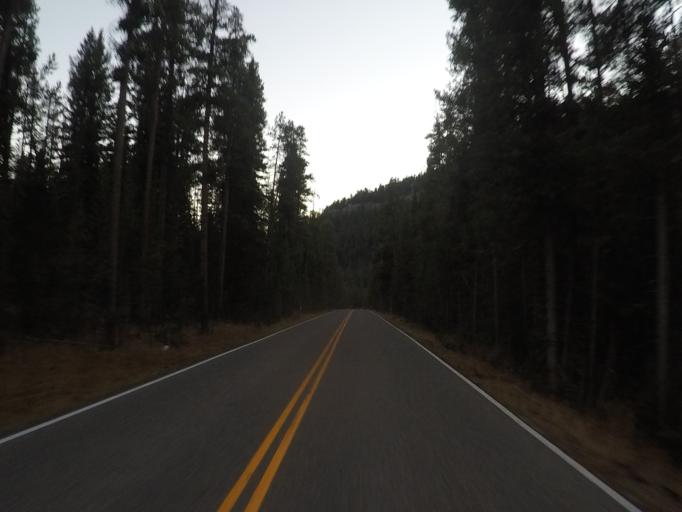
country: US
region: Montana
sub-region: Stillwater County
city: Absarokee
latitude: 44.9477
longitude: -110.0799
